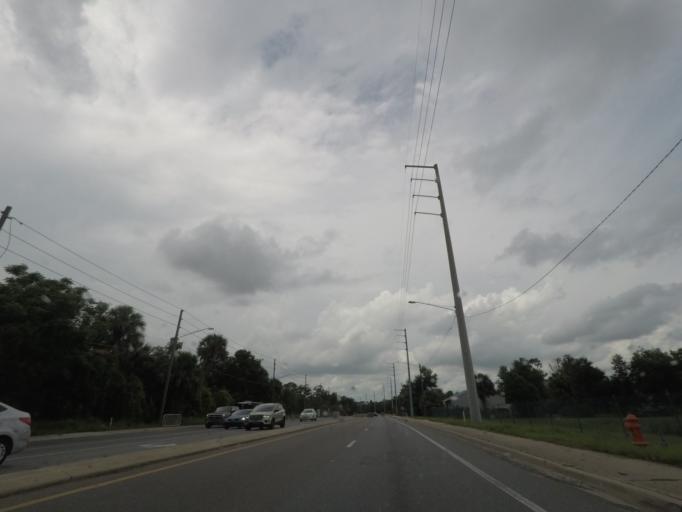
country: US
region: Florida
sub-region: Polk County
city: Loughman
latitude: 28.2419
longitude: -81.5671
